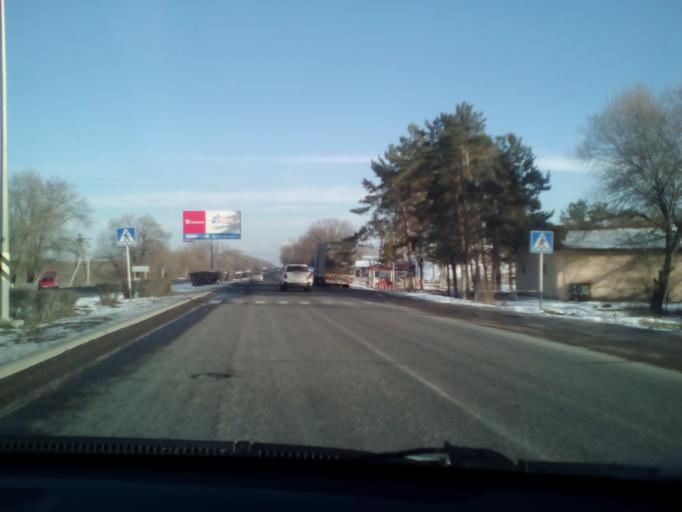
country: KZ
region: Almaty Oblysy
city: Burunday
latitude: 43.2224
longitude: 76.4262
